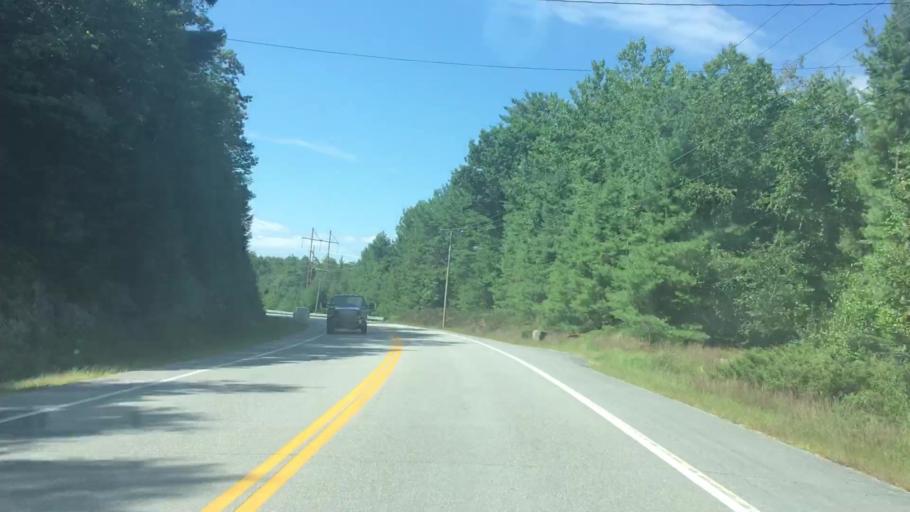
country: US
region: Maine
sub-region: Kennebec County
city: Monmouth
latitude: 44.1930
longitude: -69.9697
